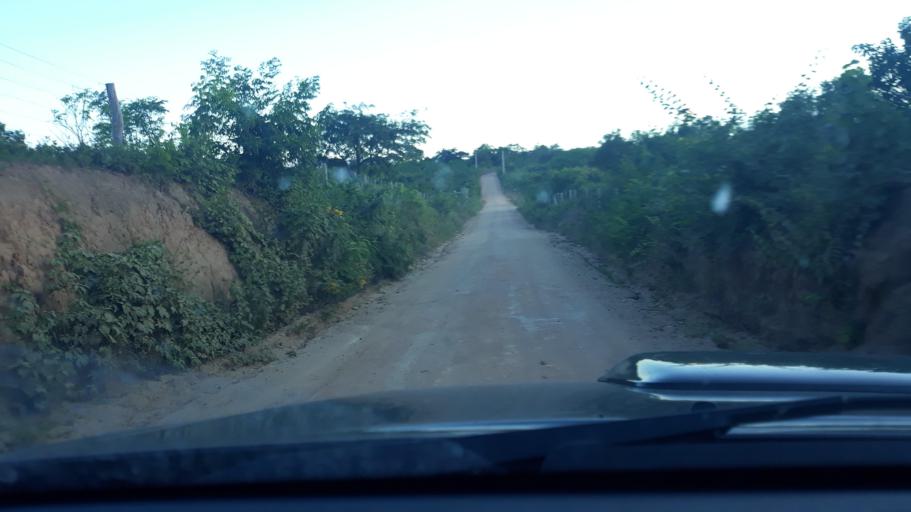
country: BR
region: Bahia
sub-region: Riacho De Santana
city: Riacho de Santana
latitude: -13.8020
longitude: -42.7126
